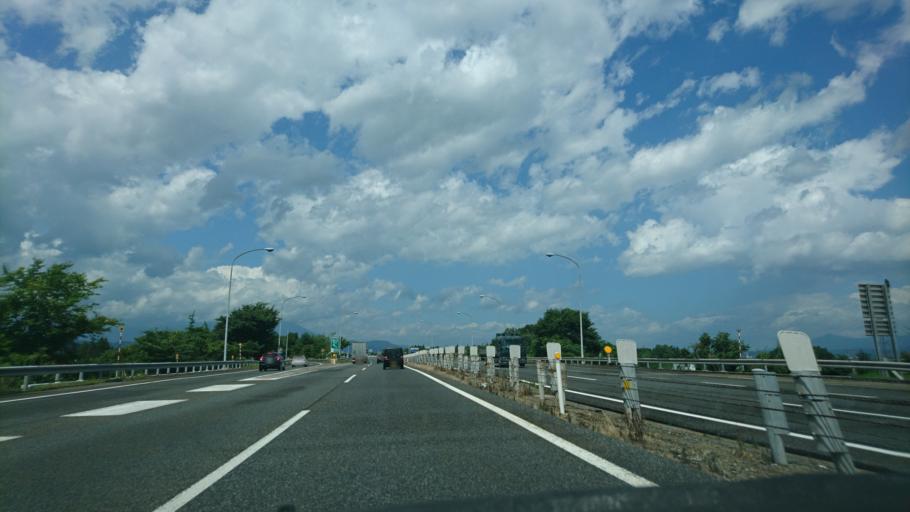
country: JP
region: Iwate
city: Morioka-shi
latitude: 39.6491
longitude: 141.1239
